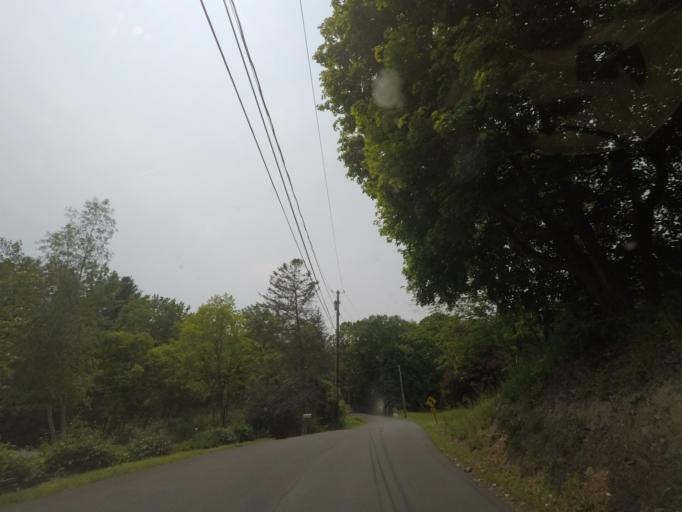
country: US
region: New York
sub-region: Rensselaer County
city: East Greenbush
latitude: 42.5491
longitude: -73.6916
